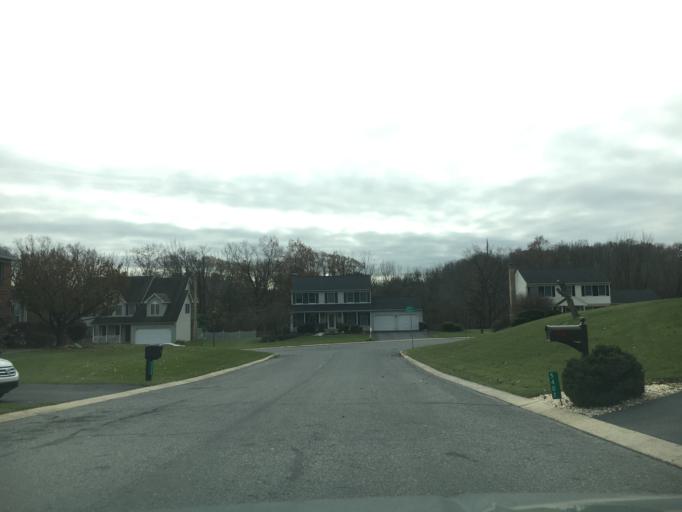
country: US
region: Pennsylvania
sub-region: Lehigh County
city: Laurys Station
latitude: 40.7216
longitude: -75.5334
